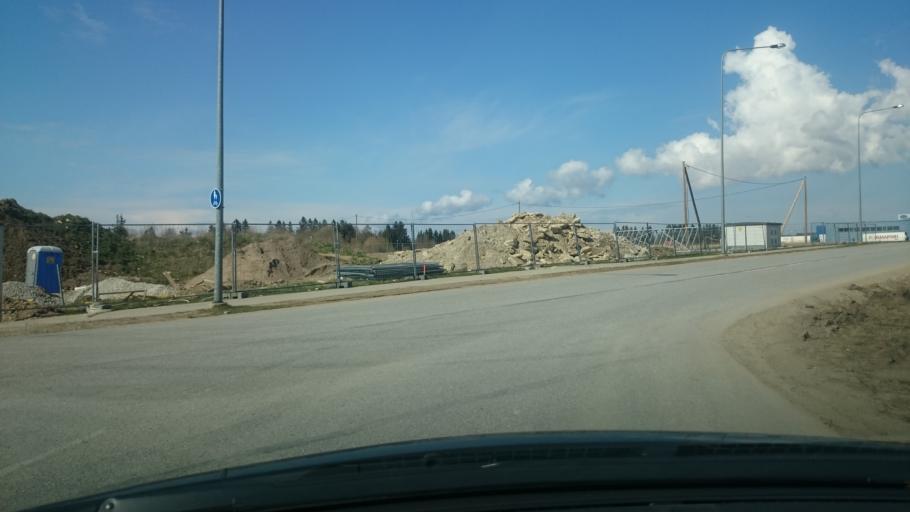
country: EE
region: Harju
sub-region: Rae vald
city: Jueri
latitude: 59.3645
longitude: 24.8681
